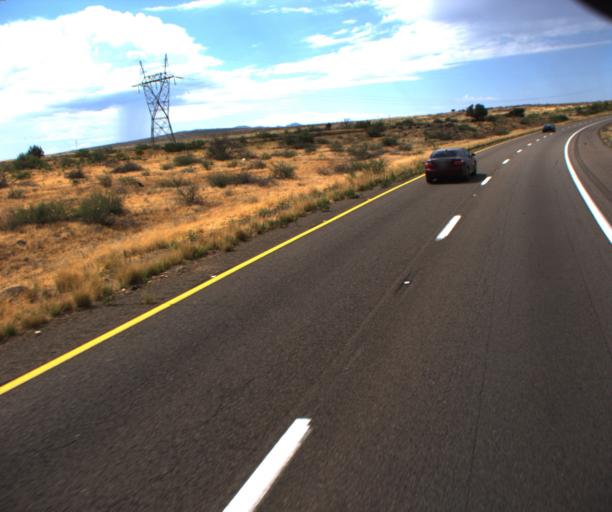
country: US
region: Arizona
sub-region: Yavapai County
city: Cordes Lakes
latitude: 34.2197
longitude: -112.1115
